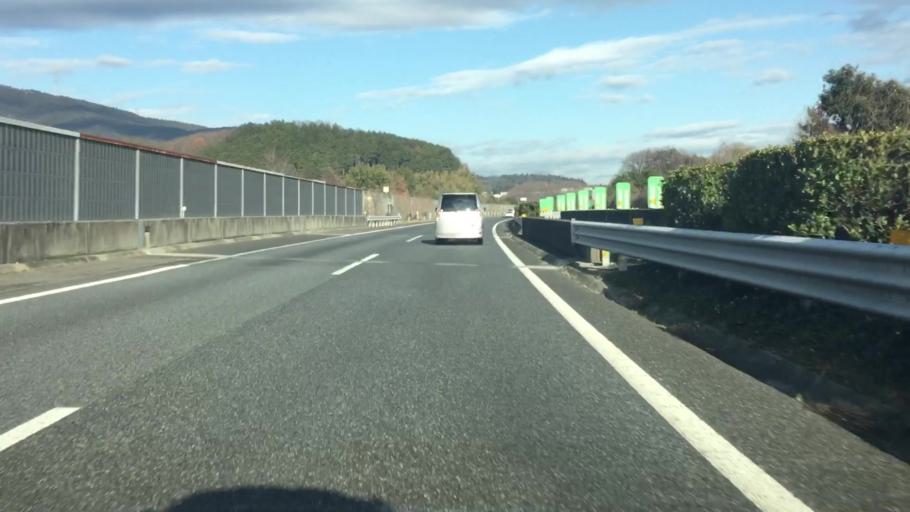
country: JP
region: Gunma
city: Tomioka
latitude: 36.2412
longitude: 138.8168
